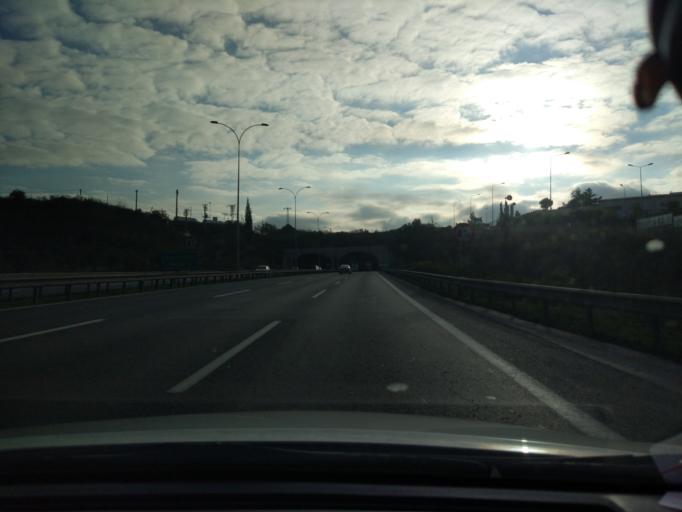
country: TR
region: Kocaeli
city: Tavsancil
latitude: 40.7755
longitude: 29.5463
